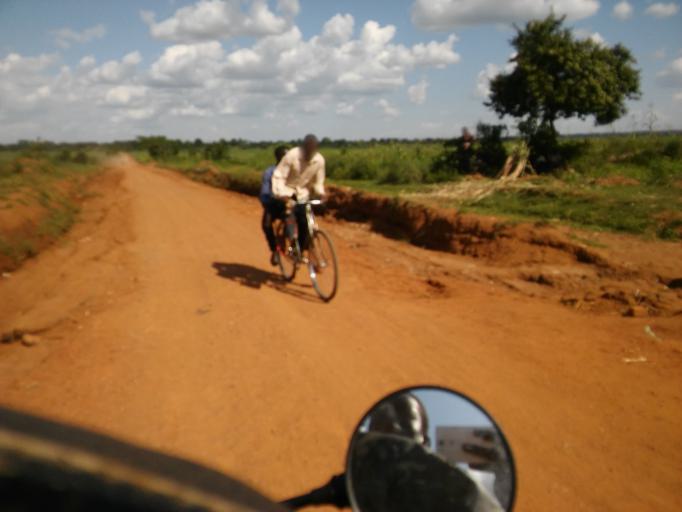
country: UG
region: Eastern Region
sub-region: Pallisa District
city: Pallisa
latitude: 1.1384
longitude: 33.7258
